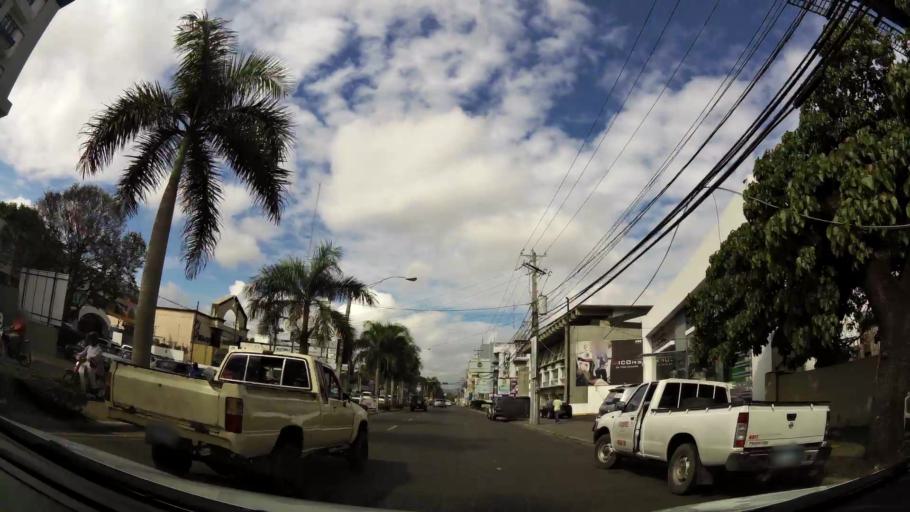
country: DO
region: Santiago
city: Santiago de los Caballeros
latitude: 19.4603
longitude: -70.6908
